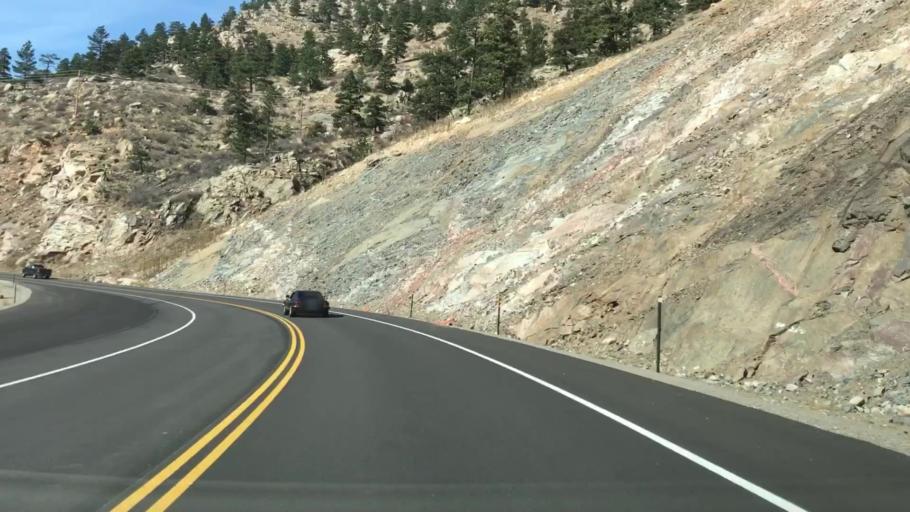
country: US
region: Colorado
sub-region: Boulder County
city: Lyons
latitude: 40.4301
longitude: -105.3087
